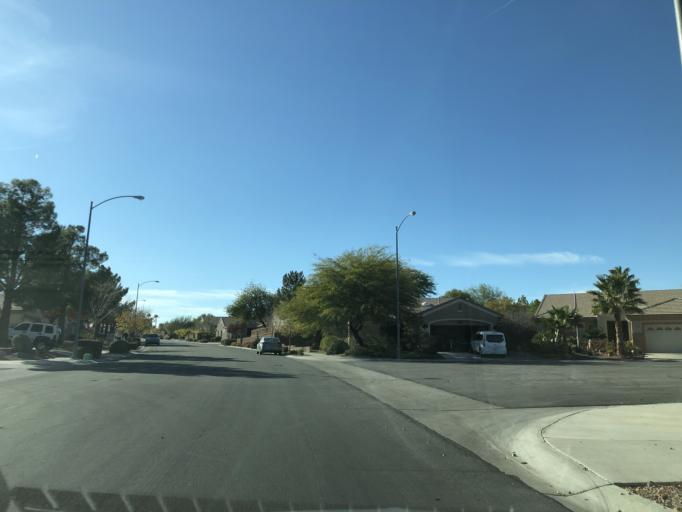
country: US
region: Nevada
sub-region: Clark County
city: Whitney
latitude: 36.0124
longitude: -115.0738
